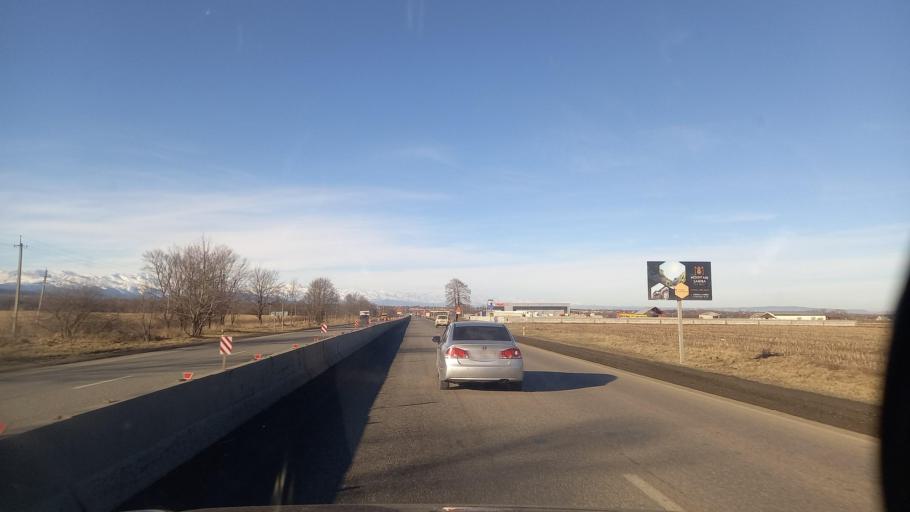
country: RU
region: North Ossetia
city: Vladikavkaz
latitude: 43.0261
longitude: 44.6208
